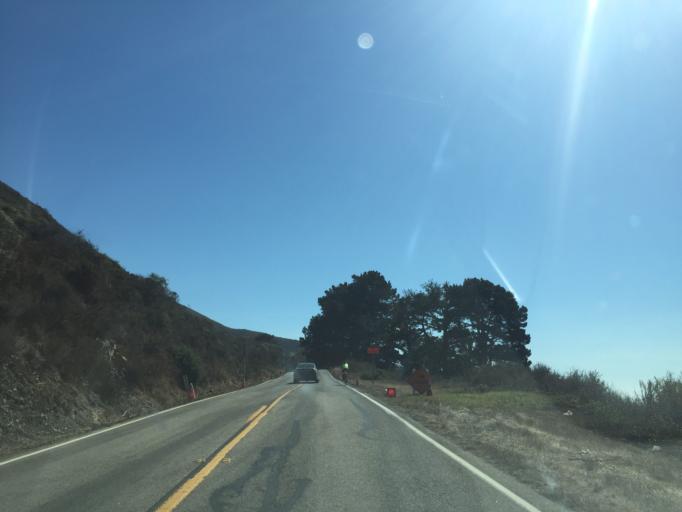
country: US
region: California
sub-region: Monterey County
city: Greenfield
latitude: 36.0578
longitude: -121.5904
